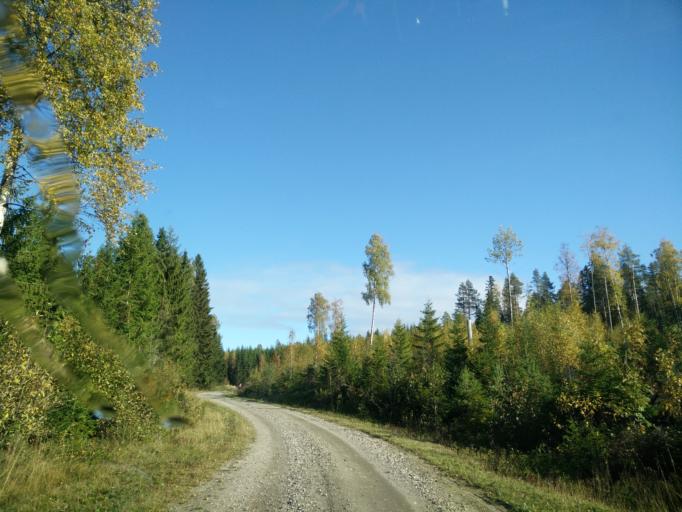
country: SE
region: Vaesternorrland
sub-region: Sundsvalls Kommun
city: Matfors
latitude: 62.3347
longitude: 16.8599
